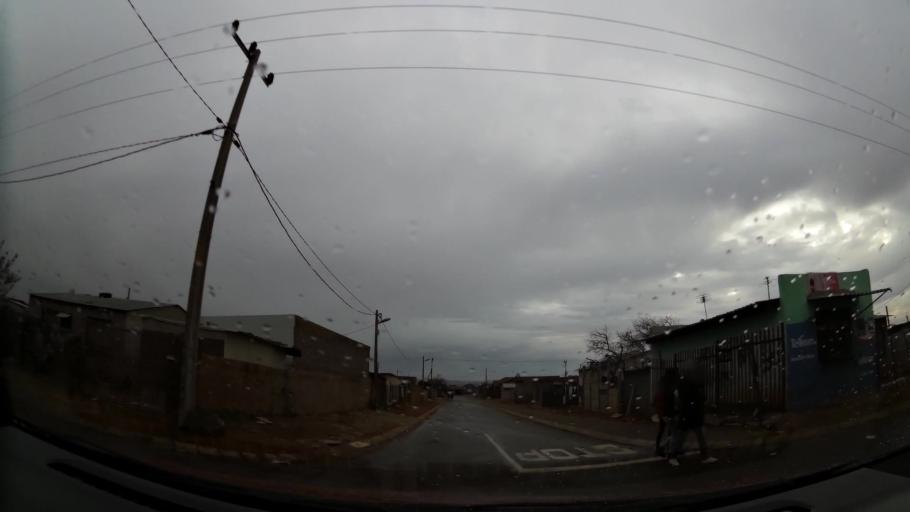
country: ZA
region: Gauteng
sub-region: City of Johannesburg Metropolitan Municipality
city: Roodepoort
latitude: -26.1759
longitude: 27.7888
